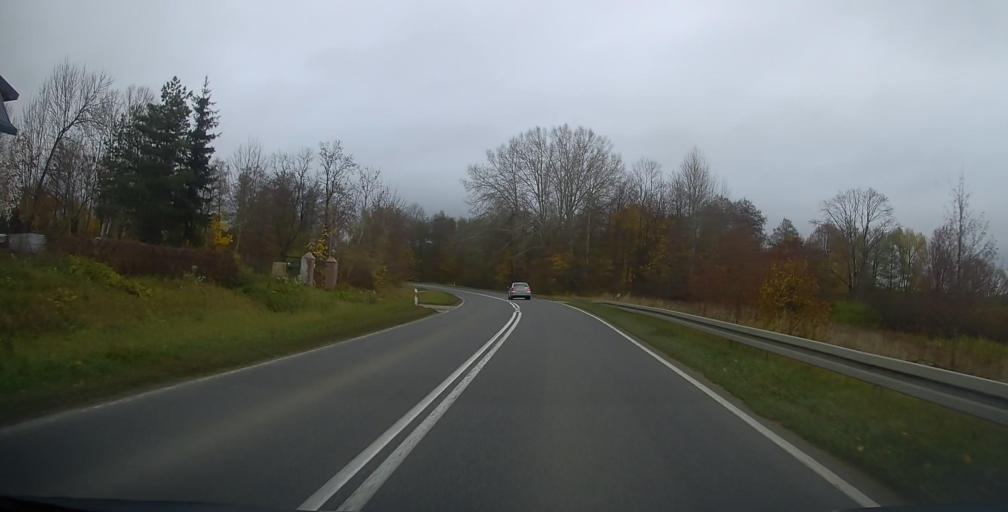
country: PL
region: Warmian-Masurian Voivodeship
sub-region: Powiat elcki
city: Elk
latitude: 53.8467
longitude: 22.4708
